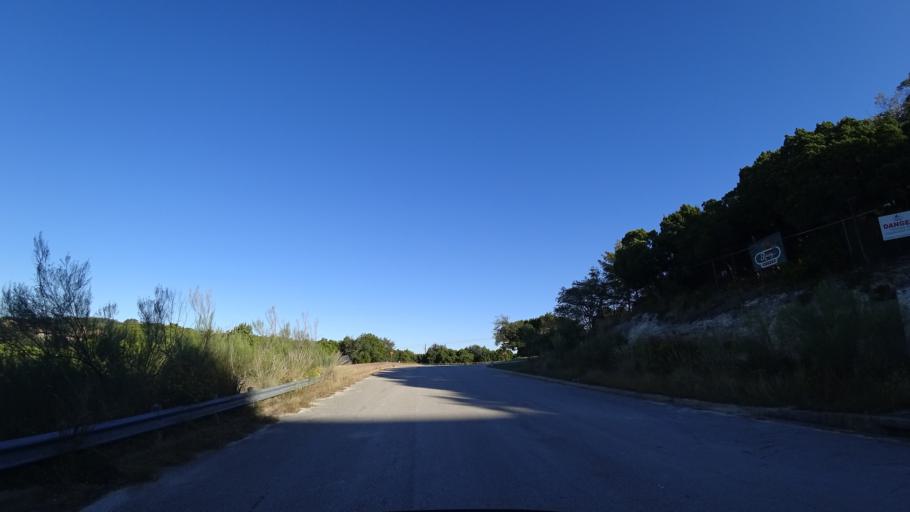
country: US
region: Texas
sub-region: Travis County
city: West Lake Hills
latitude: 30.3611
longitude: -97.8112
